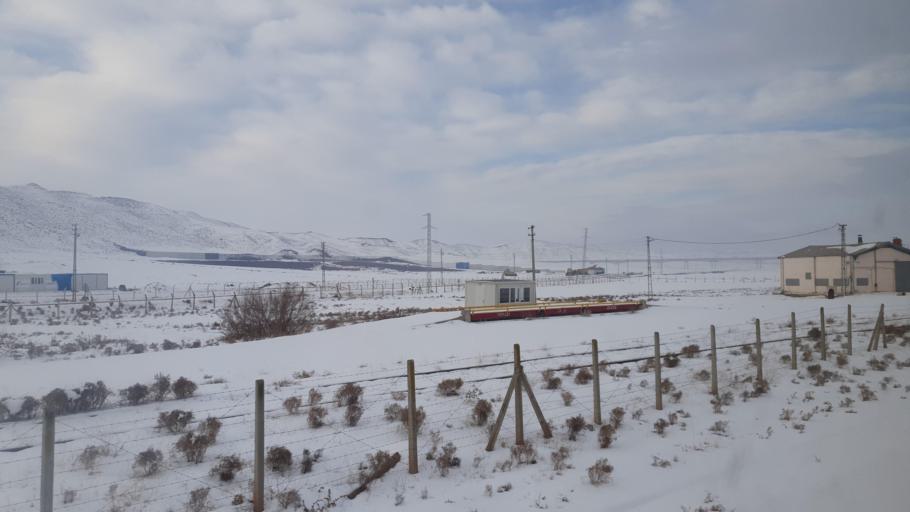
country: TR
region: Kirikkale
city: Delice
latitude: 39.8914
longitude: 33.9949
